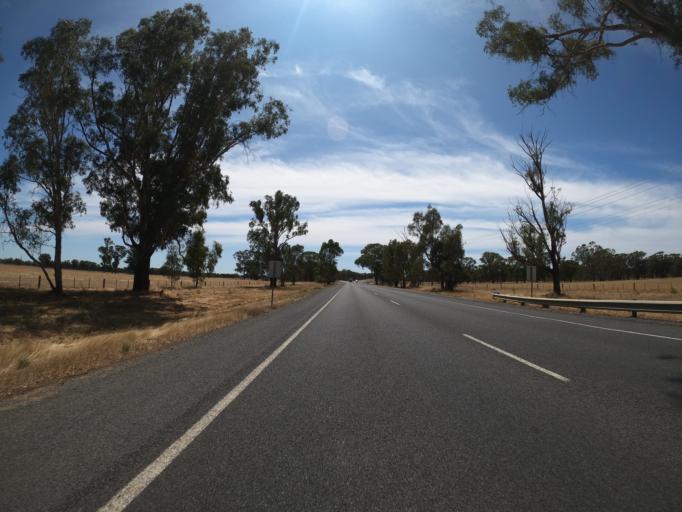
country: AU
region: Victoria
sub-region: Benalla
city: Benalla
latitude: -36.5241
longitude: 146.0554
